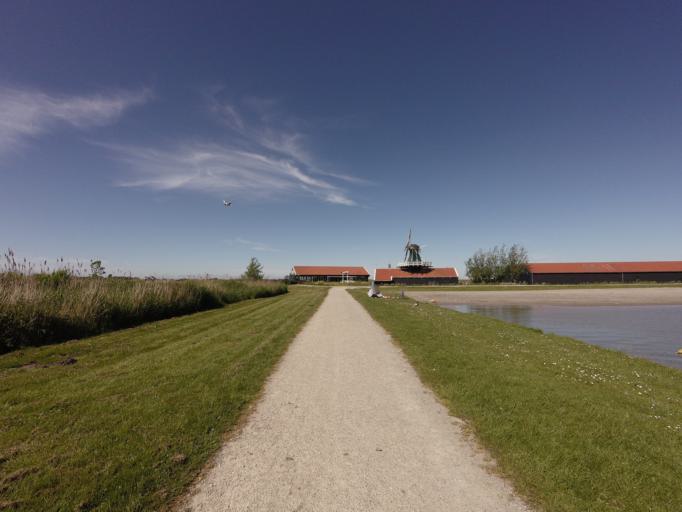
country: NL
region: North Holland
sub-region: Gemeente Uitgeest
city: Uitgeest
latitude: 52.5288
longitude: 4.7309
